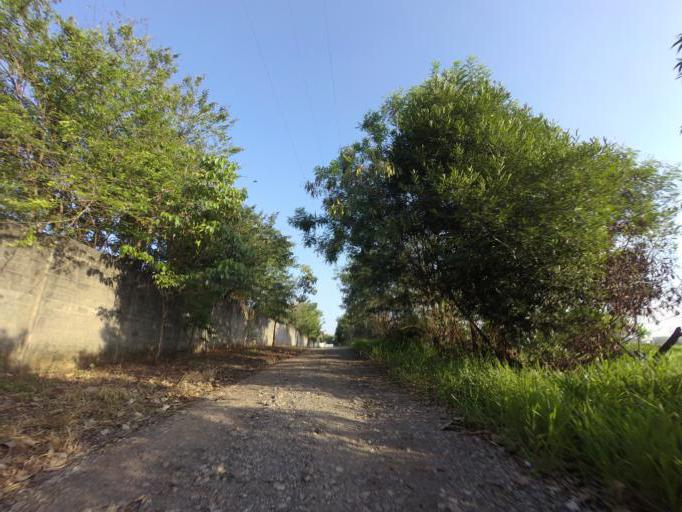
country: BR
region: Sao Paulo
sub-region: Piracicaba
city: Piracicaba
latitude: -22.7484
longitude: -47.6043
